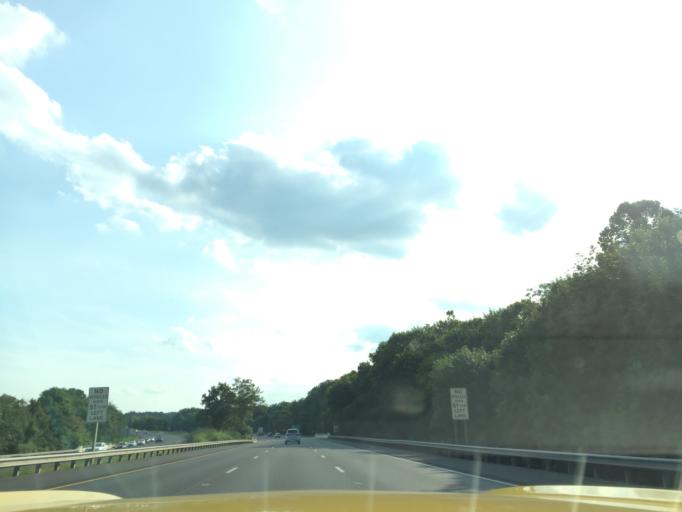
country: US
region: Maryland
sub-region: Harford County
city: Riverside
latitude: 39.4777
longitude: -76.2684
